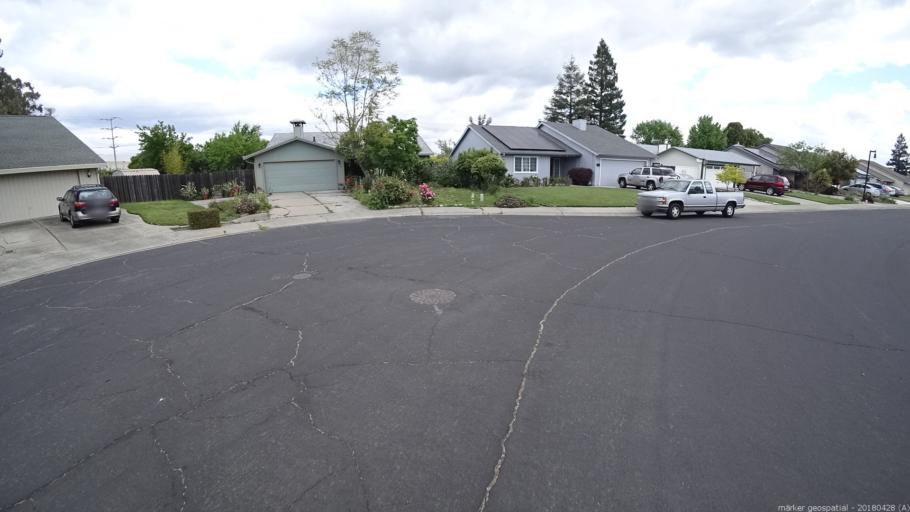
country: US
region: California
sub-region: Yolo County
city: West Sacramento
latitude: 38.5519
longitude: -121.5581
